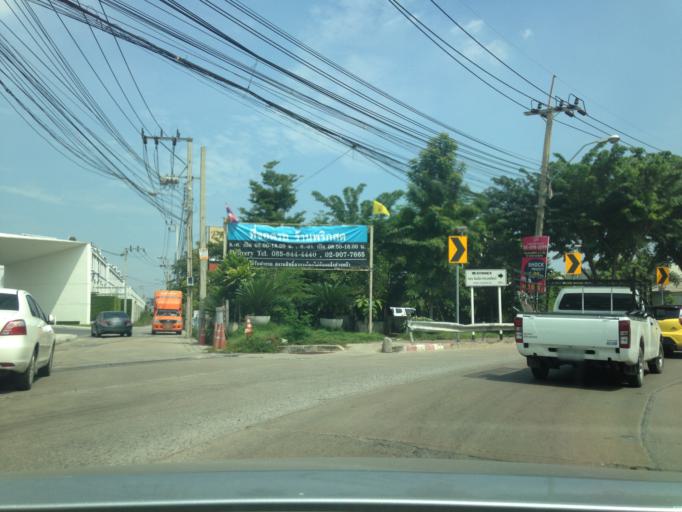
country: TH
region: Bangkok
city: Lat Phrao
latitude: 13.8357
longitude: 100.6271
